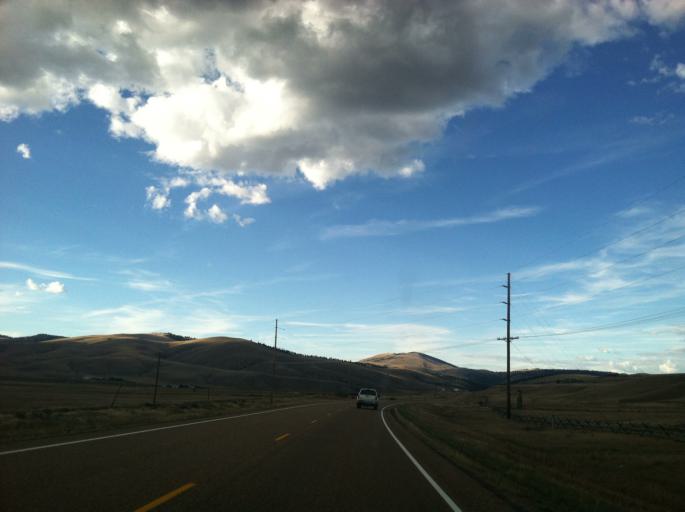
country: US
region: Montana
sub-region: Granite County
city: Philipsburg
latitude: 46.3574
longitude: -113.3148
